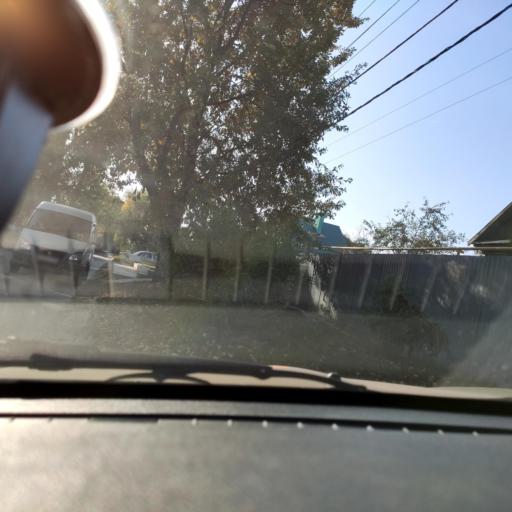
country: RU
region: Samara
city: Tol'yatti
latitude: 53.5360
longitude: 49.4089
